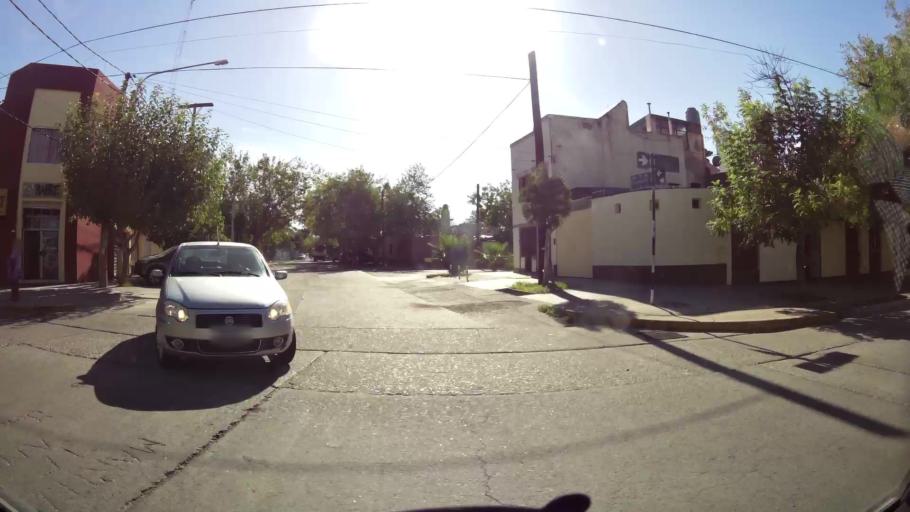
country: AR
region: Mendoza
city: Mendoza
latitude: -32.9083
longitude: -68.8320
